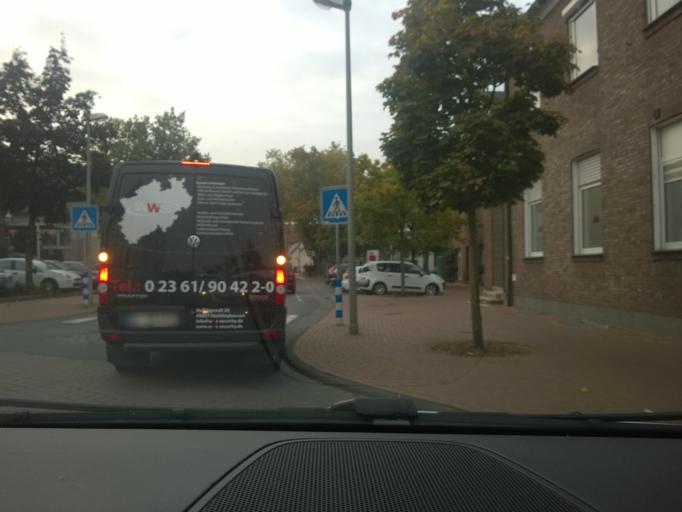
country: DE
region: North Rhine-Westphalia
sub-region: Regierungsbezirk Munster
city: Sudlohn
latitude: 51.9450
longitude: 6.8677
